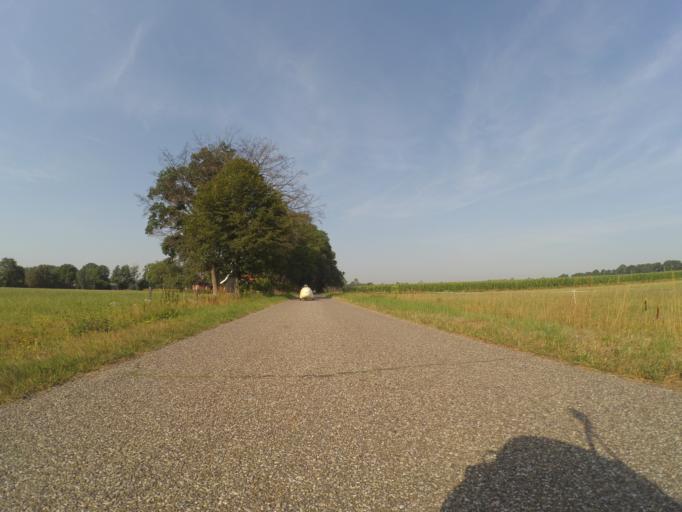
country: NL
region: Overijssel
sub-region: Gemeente Oldenzaal
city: Oldenzaal
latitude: 52.3665
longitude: 6.8625
